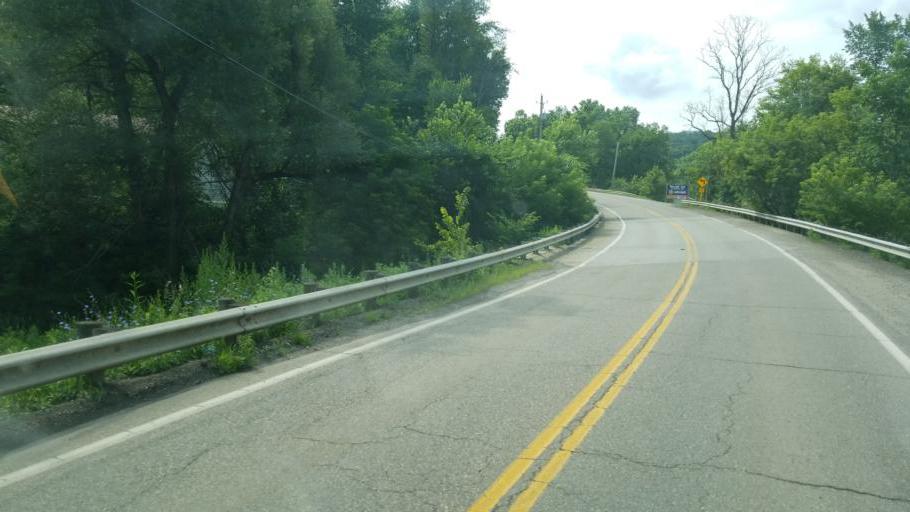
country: US
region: Ohio
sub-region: Columbiana County
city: Salineville
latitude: 40.6244
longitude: -80.8243
